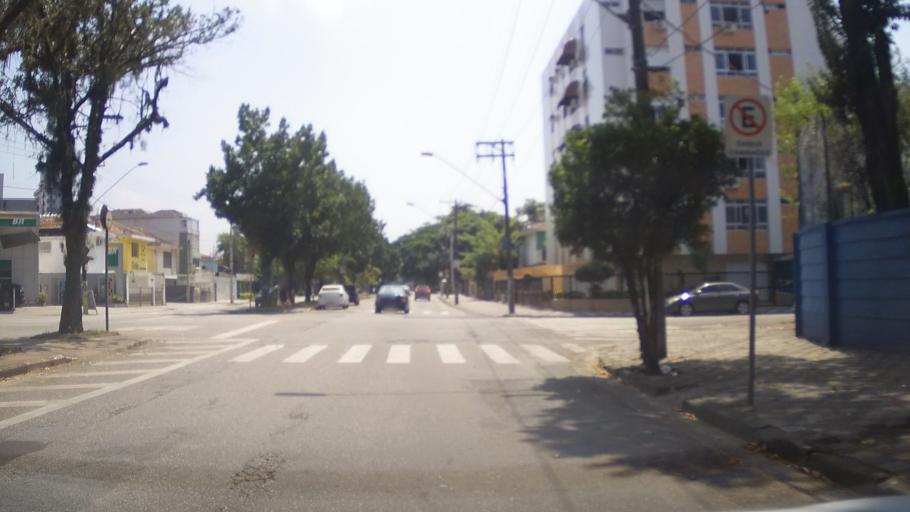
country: BR
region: Sao Paulo
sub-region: Santos
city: Santos
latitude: -23.9797
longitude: -46.3000
